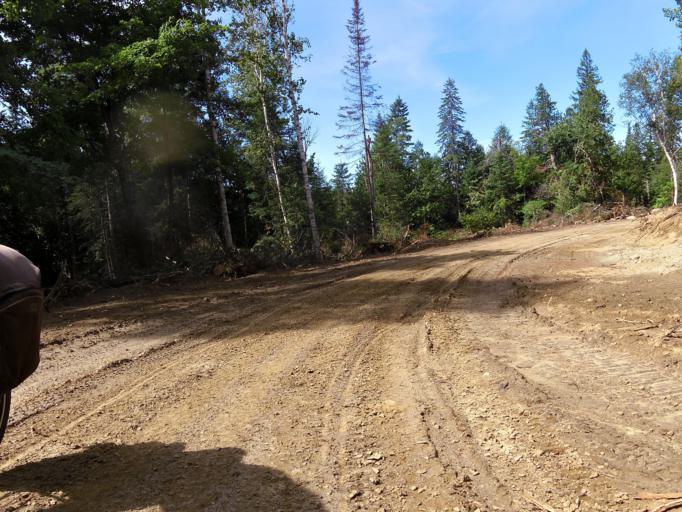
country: CA
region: Ontario
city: Renfrew
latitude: 45.1061
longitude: -76.7206
